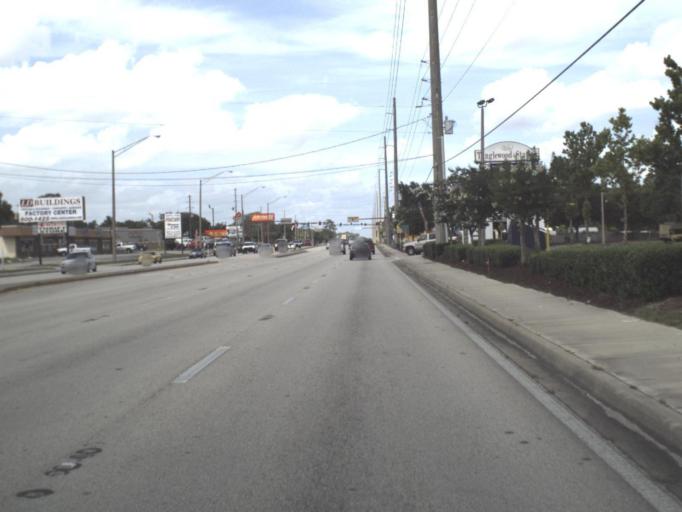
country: US
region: Florida
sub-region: Clay County
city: Lakeside
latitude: 30.1264
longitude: -81.7930
